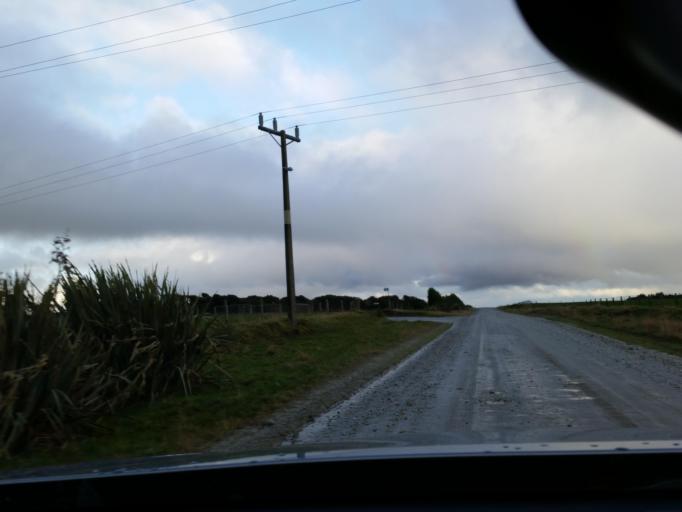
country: NZ
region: Southland
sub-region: Invercargill City
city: Invercargill
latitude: -46.4341
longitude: 168.5062
